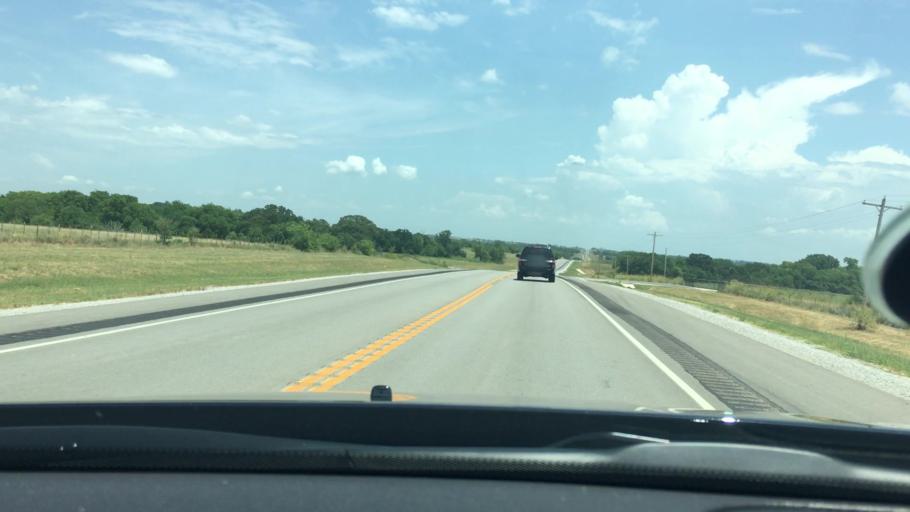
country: US
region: Oklahoma
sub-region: Love County
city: Marietta
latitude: 33.9399
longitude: -97.2323
